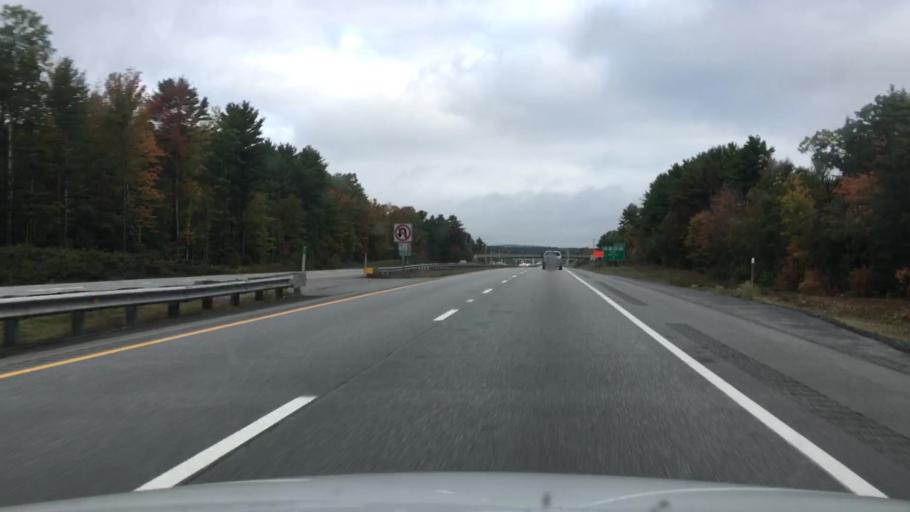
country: US
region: Maine
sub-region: Cumberland County
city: New Gloucester
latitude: 43.8745
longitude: -70.3307
